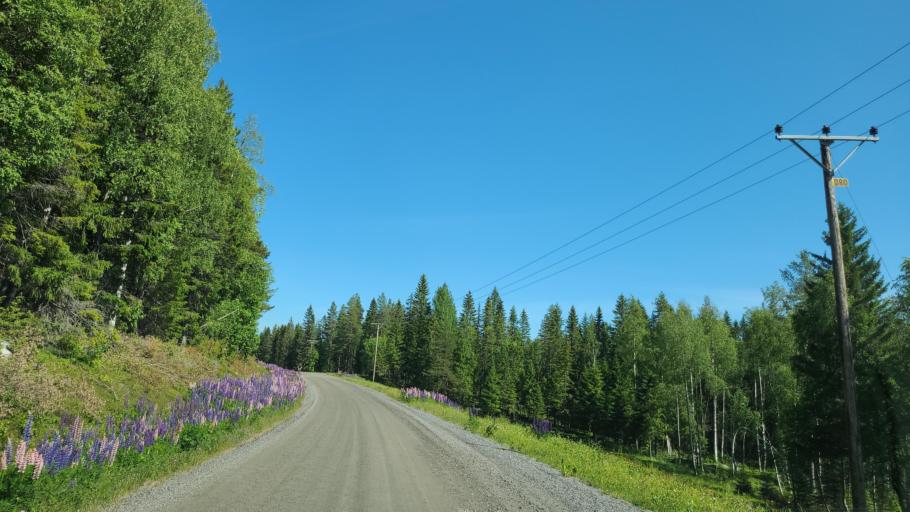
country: SE
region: Vaesterbotten
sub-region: Bjurholms Kommun
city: Bjurholm
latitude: 63.6395
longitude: 19.1471
